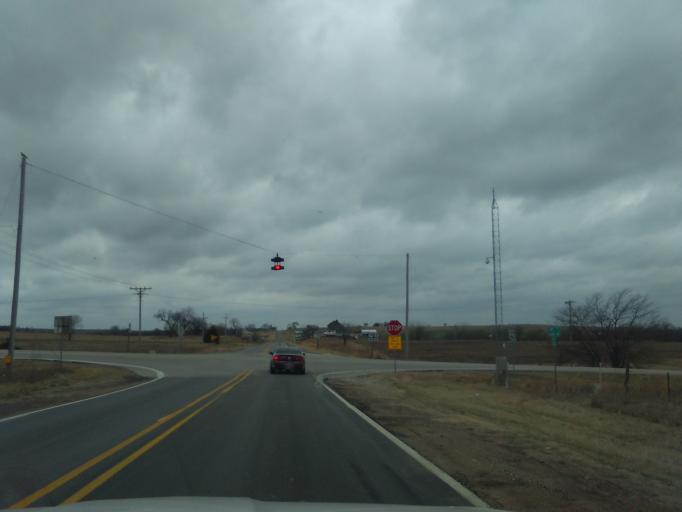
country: US
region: Kansas
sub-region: Nemaha County
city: Sabetha
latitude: 40.0586
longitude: -95.8222
